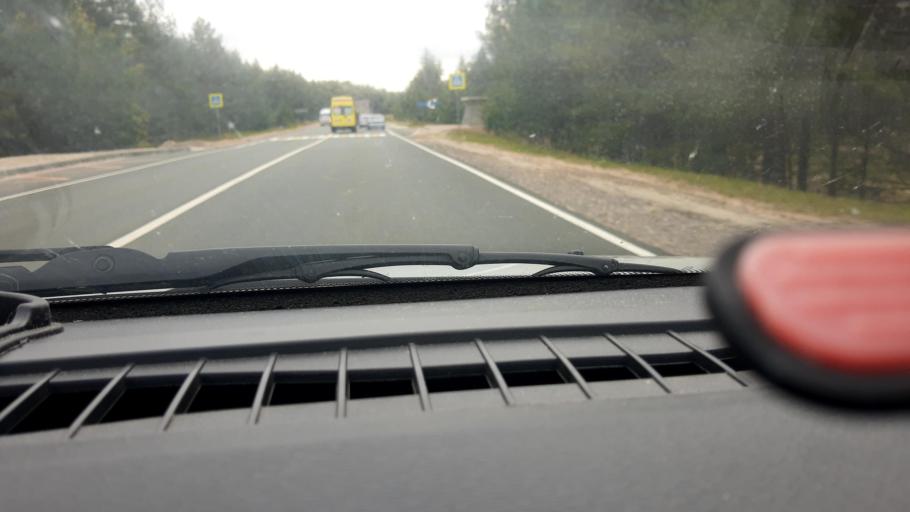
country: RU
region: Nizjnij Novgorod
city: Uren'
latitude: 57.3990
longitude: 45.6863
